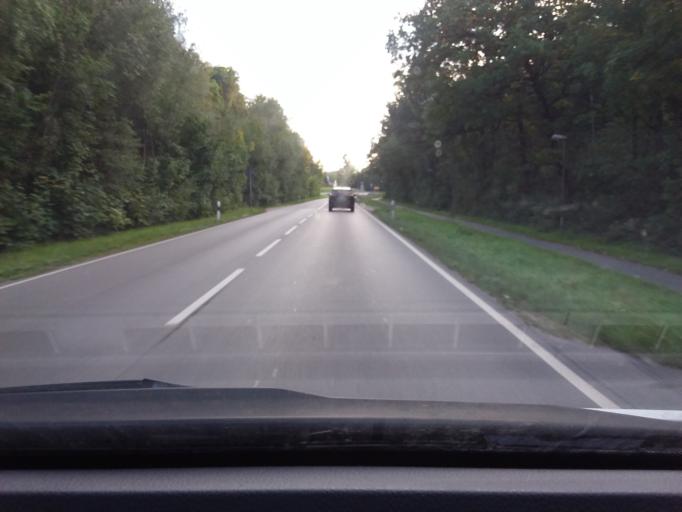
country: DE
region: Bavaria
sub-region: Upper Bavaria
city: Oberschleissheim
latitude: 48.2536
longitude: 11.5815
